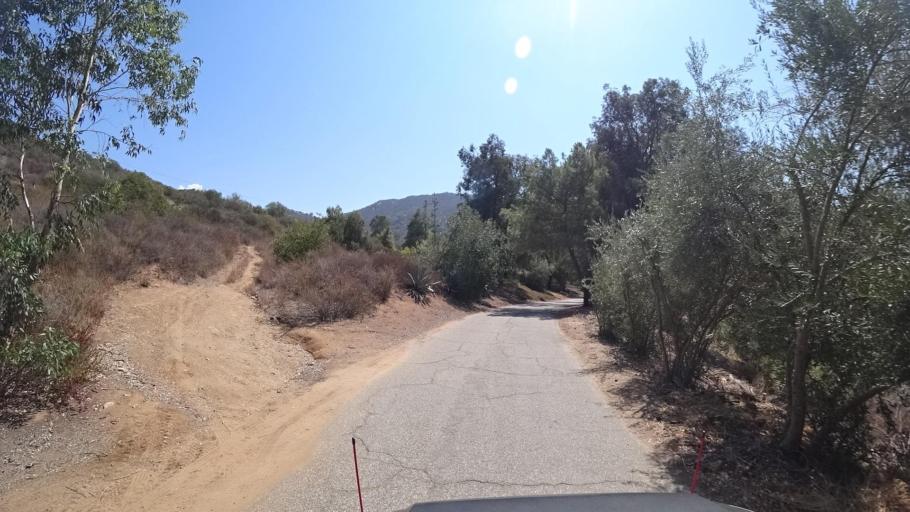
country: US
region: California
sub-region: San Diego County
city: Hidden Meadows
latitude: 33.2491
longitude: -117.1102
